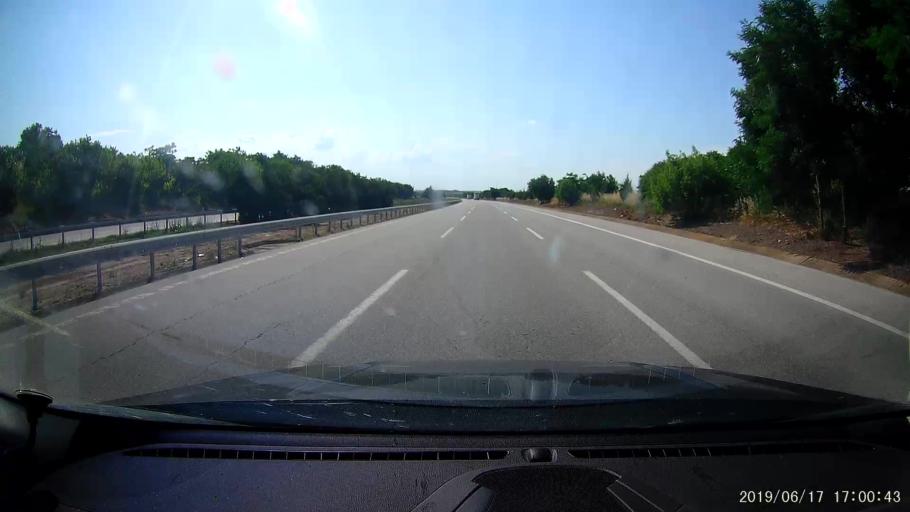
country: TR
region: Edirne
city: Haskoy
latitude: 41.6234
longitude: 26.8238
